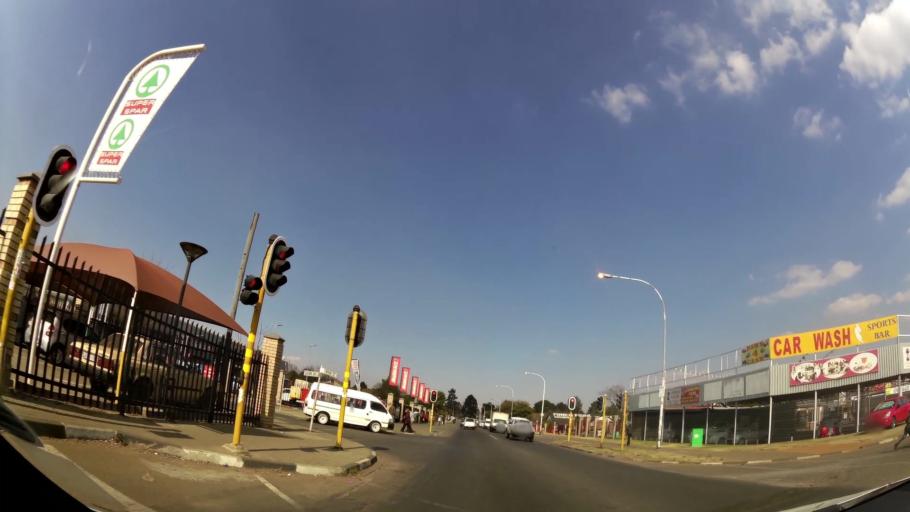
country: ZA
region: Gauteng
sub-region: Ekurhuleni Metropolitan Municipality
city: Germiston
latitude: -26.1916
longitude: 28.2048
